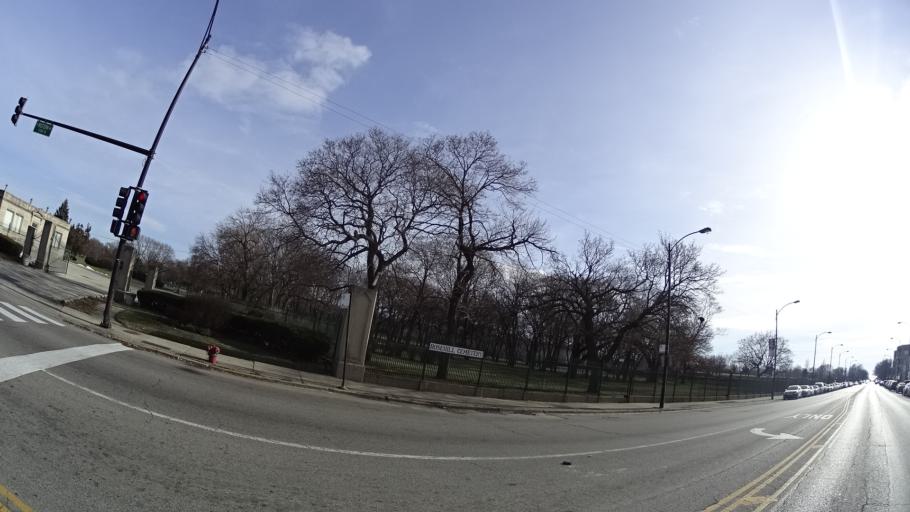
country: US
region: Illinois
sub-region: Cook County
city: Lincolnwood
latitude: 41.9831
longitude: -87.6895
